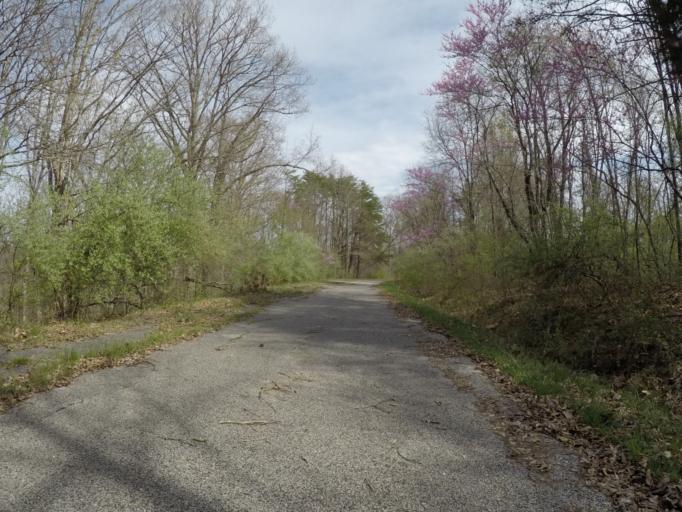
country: US
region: West Virginia
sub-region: Wayne County
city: Lavalette
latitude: 38.3199
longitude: -82.3511
